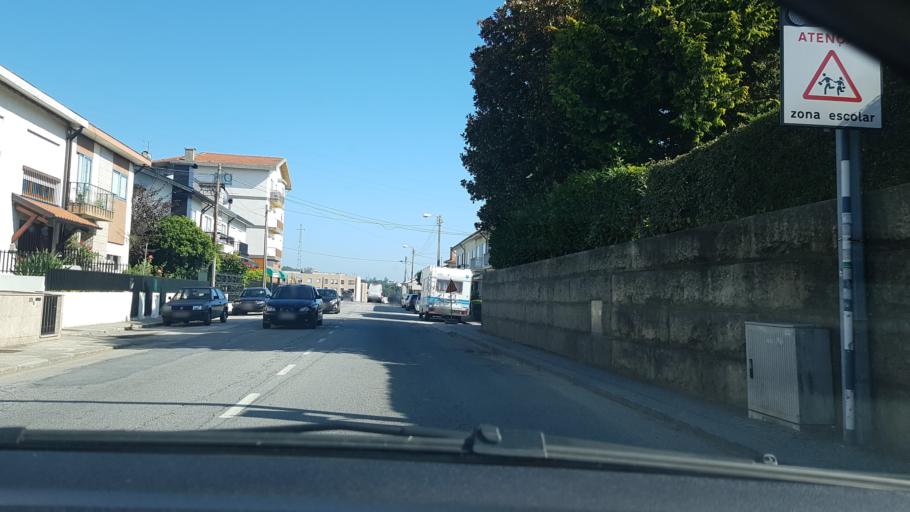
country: PT
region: Porto
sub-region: Gondomar
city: Baguim do Monte
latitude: 41.1850
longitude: -8.5401
